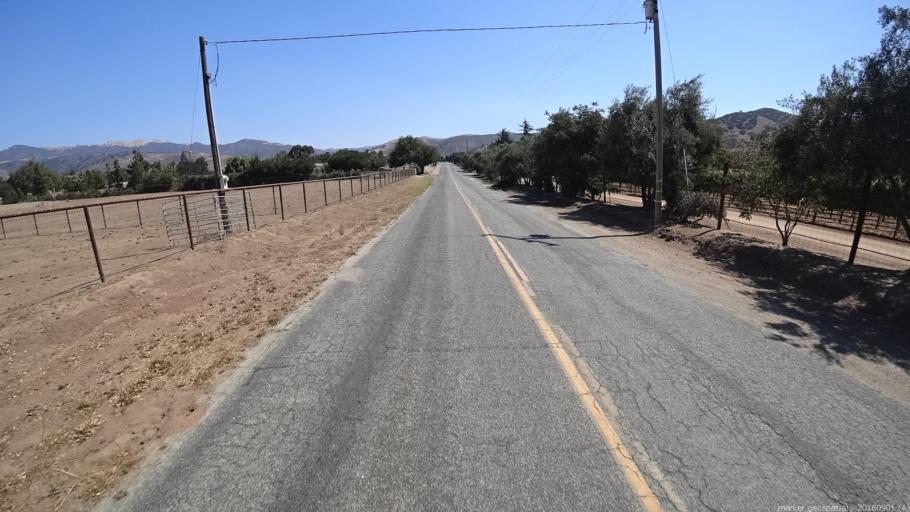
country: US
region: California
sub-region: Monterey County
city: Chualar
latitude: 36.5903
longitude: -121.4569
